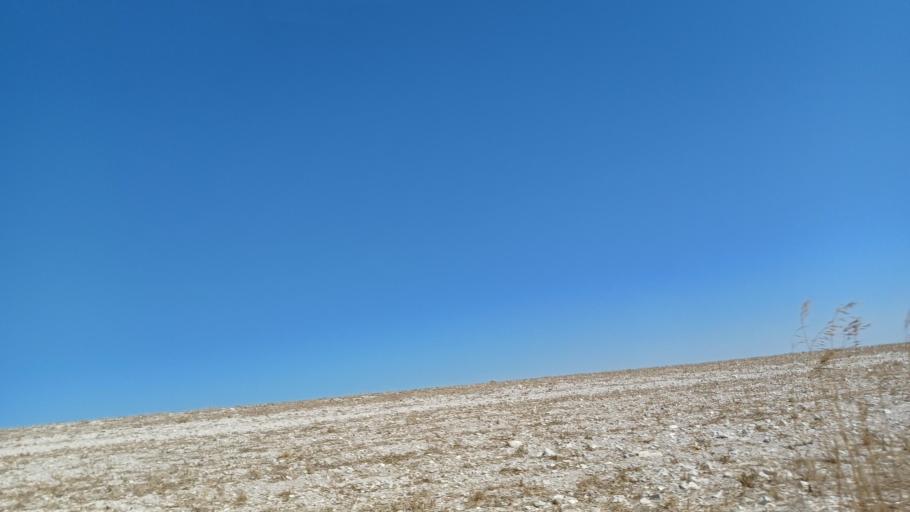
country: CY
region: Lefkosia
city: Lympia
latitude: 34.9771
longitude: 33.4832
